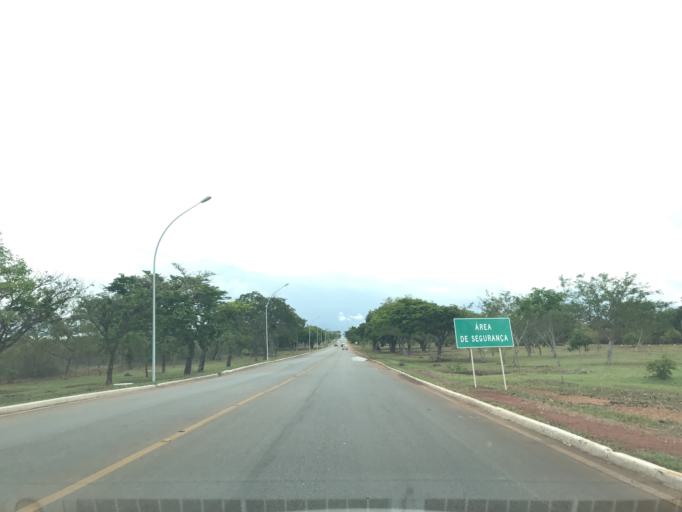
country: BR
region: Federal District
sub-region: Brasilia
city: Brasilia
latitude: -15.7943
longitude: -47.8367
